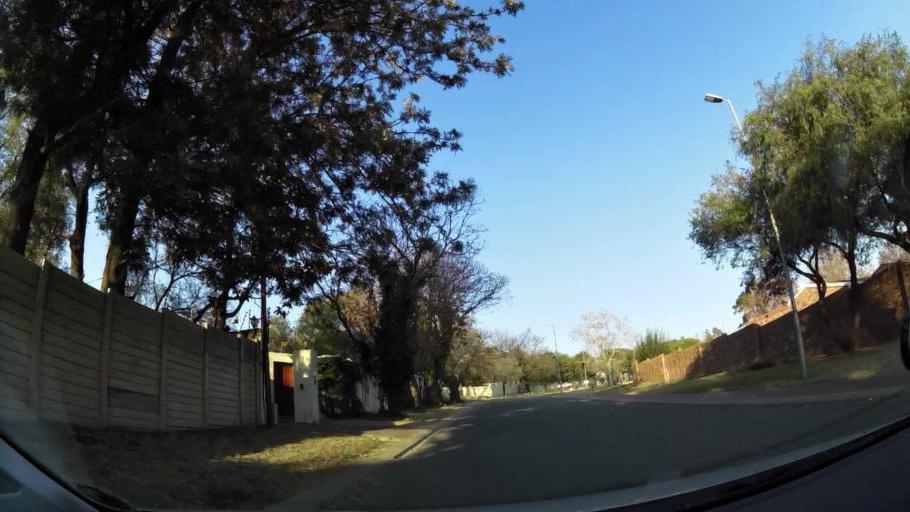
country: ZA
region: Gauteng
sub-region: City of Johannesburg Metropolitan Municipality
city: Modderfontein
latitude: -26.0781
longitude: 28.0919
